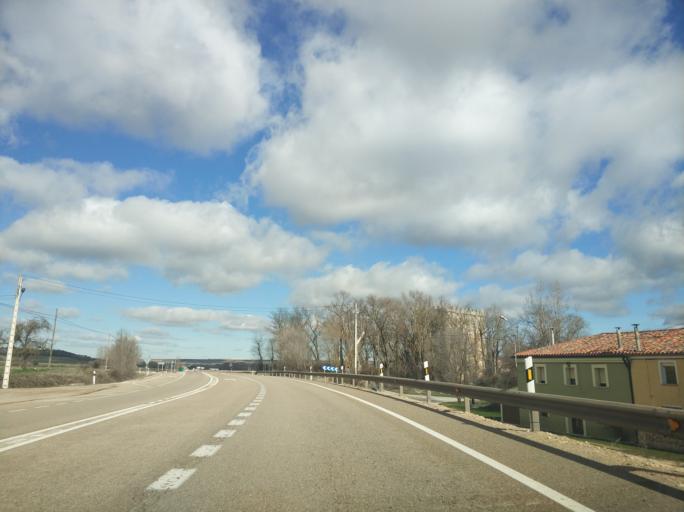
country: ES
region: Castille and Leon
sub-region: Provincia de Burgos
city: Revillarruz
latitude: 42.2357
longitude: -3.6676
